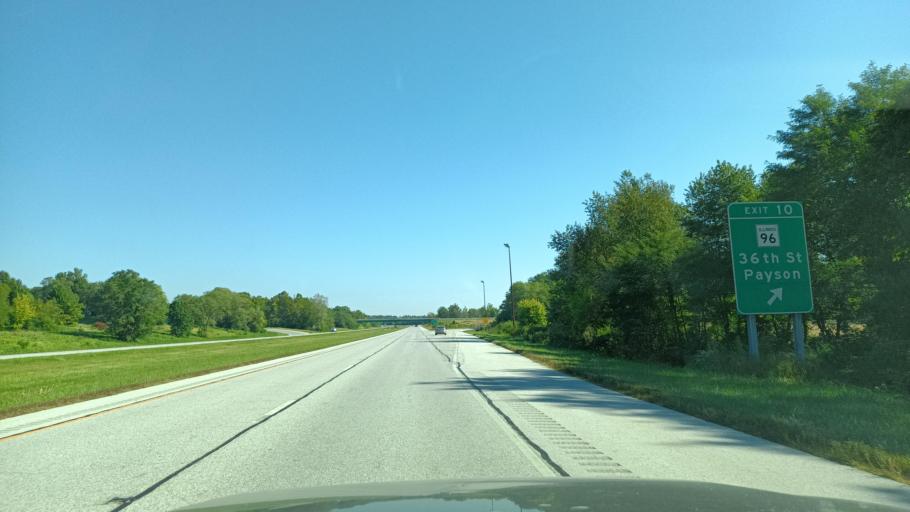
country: US
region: Illinois
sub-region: Adams County
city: Quincy
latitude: 39.8769
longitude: -91.3347
